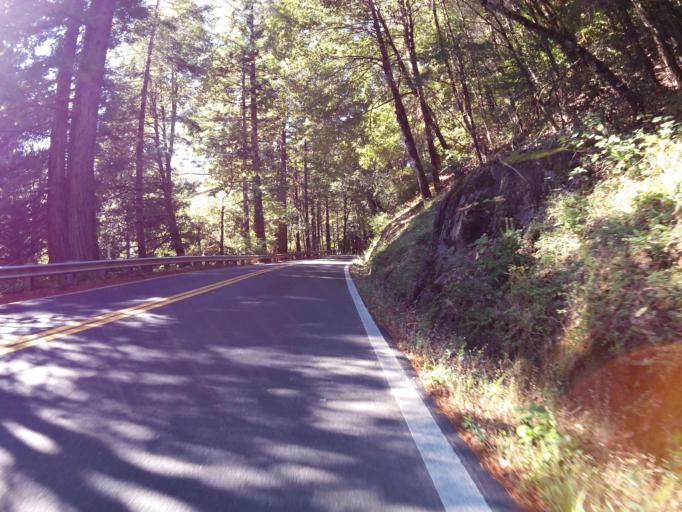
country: US
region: California
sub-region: Humboldt County
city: Redway
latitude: 39.8626
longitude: -123.7249
